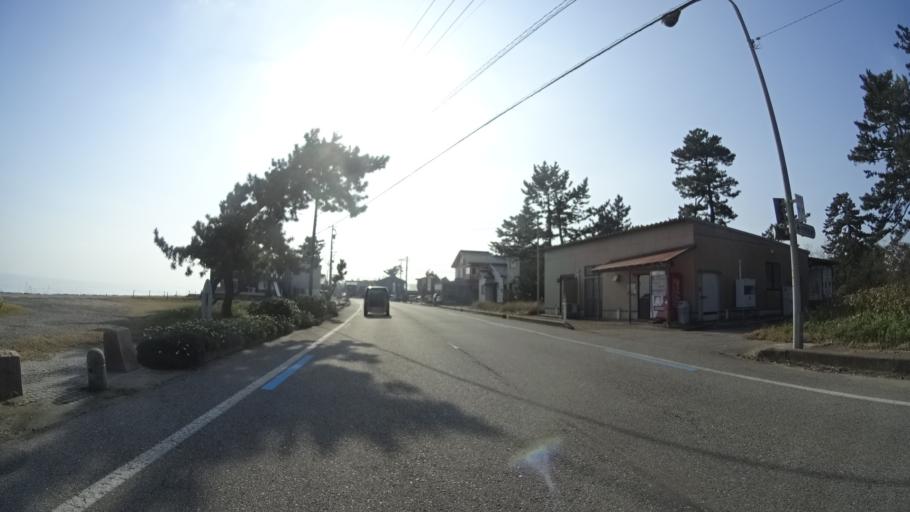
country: JP
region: Toyama
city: Himi
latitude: 36.8460
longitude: 136.9962
